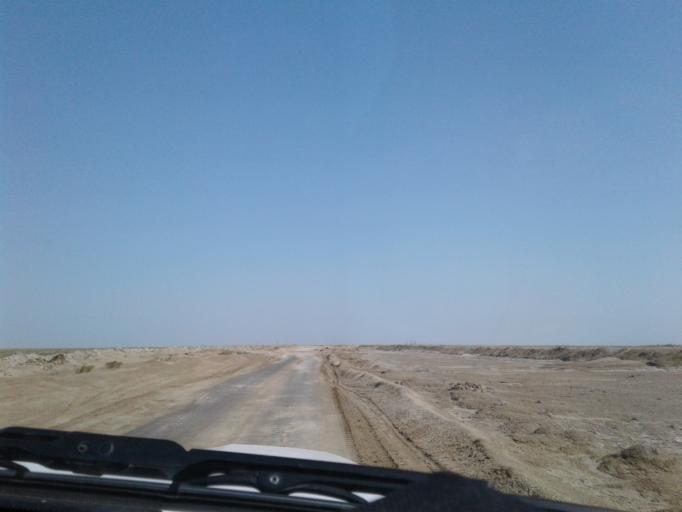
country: IR
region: Golestan
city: Gomishan
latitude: 37.8299
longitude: 53.9215
